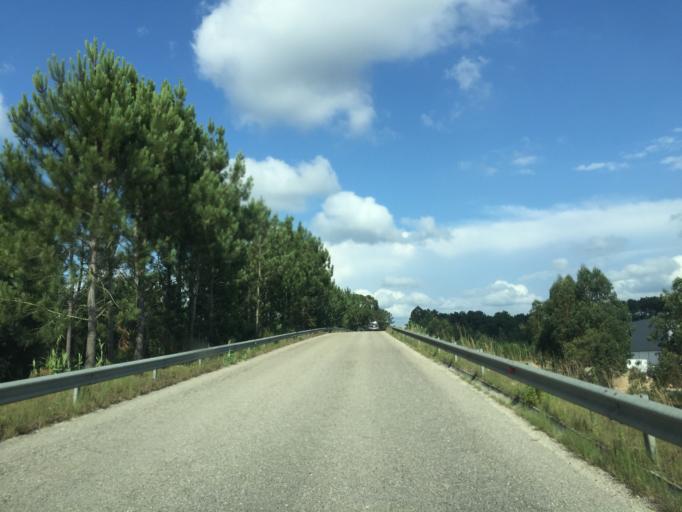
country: PT
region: Leiria
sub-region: Leiria
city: Monte Redondo
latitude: 39.9458
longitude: -8.8043
